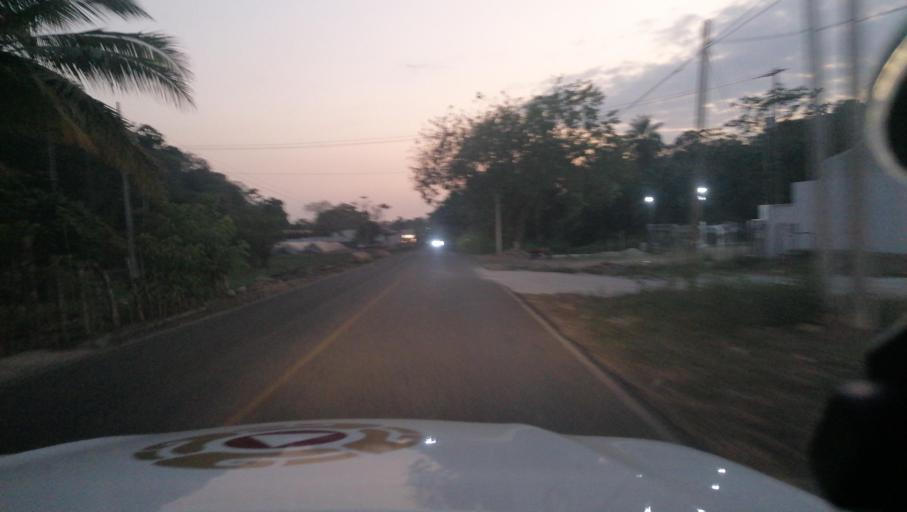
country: MX
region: Chiapas
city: Veinte de Noviembre
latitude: 14.9749
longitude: -92.2495
